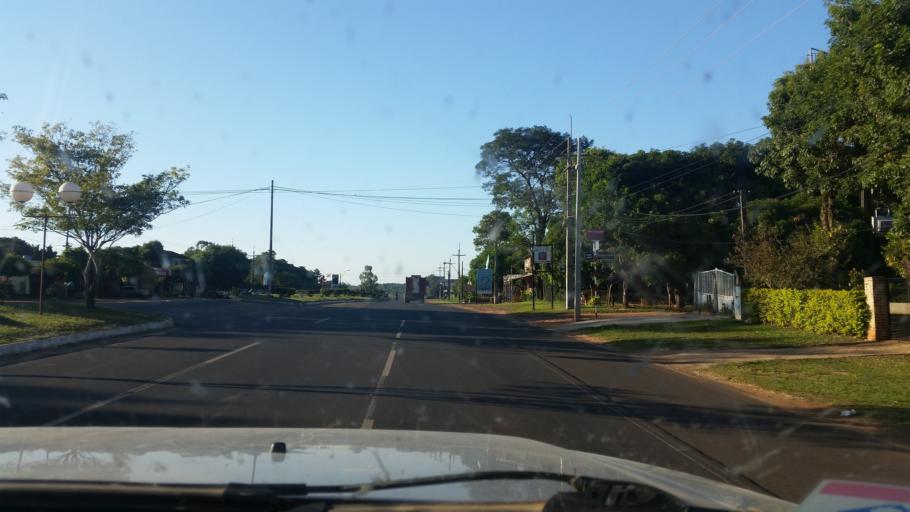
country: PY
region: Misiones
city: Santa Maria
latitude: -26.8796
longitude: -57.0320
